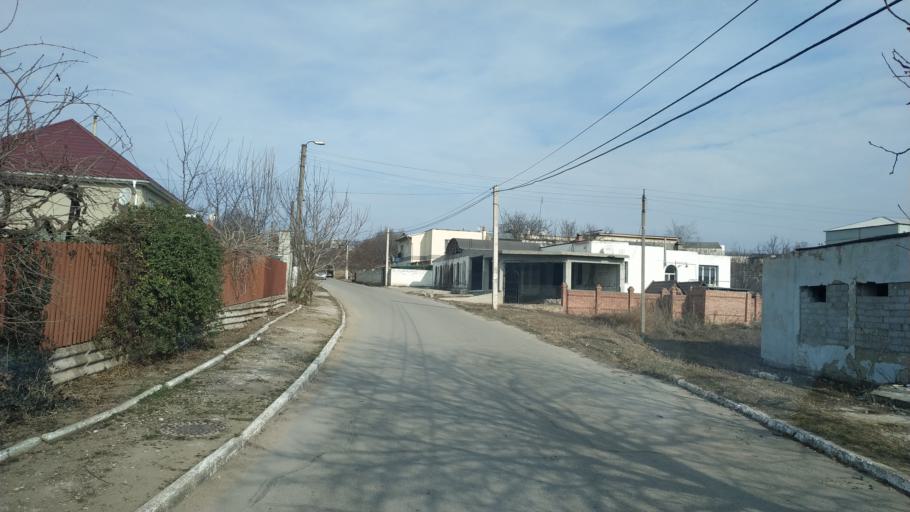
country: MD
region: Chisinau
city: Singera
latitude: 46.9259
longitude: 29.0660
